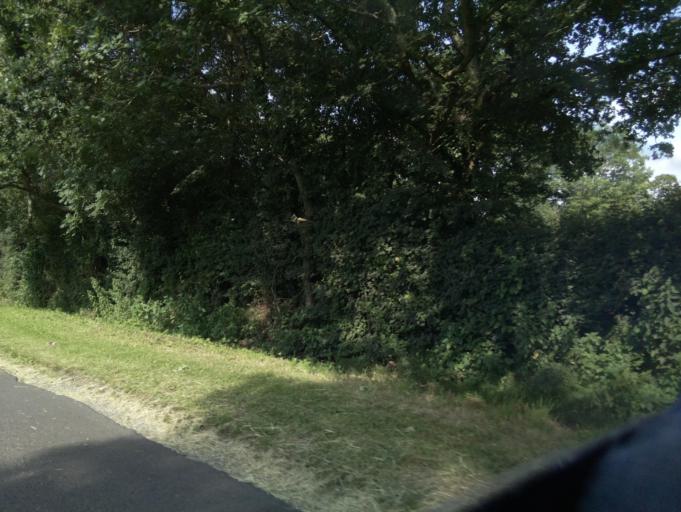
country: GB
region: England
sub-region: Wiltshire
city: Minety
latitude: 51.6354
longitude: -1.9760
